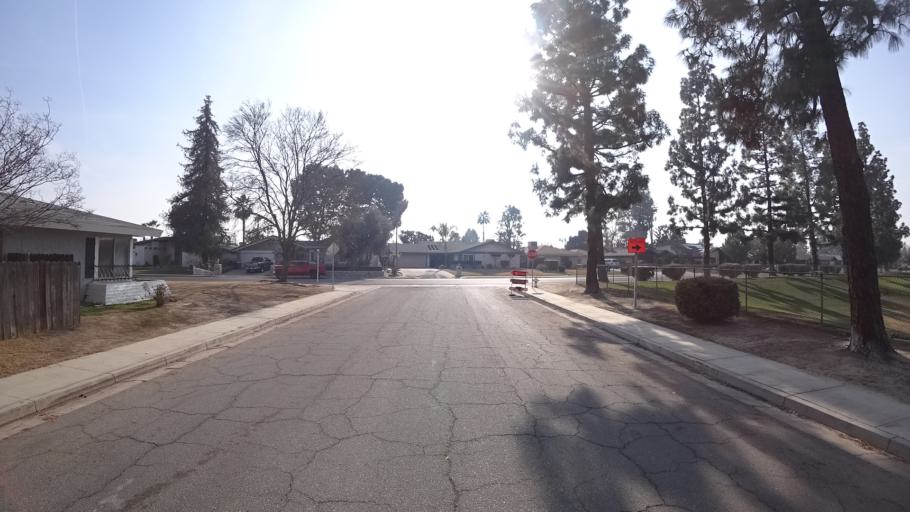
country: US
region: California
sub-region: Kern County
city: Bakersfield
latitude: 35.3592
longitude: -119.0532
